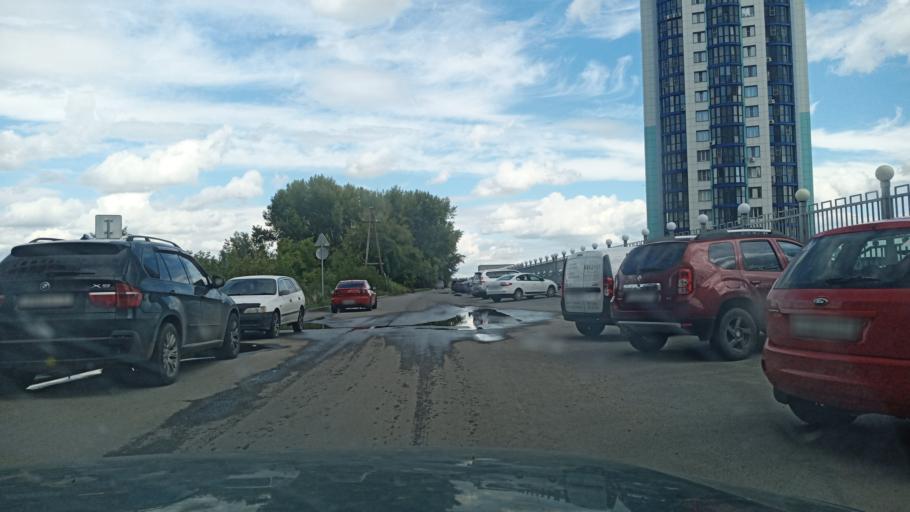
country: RU
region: Altai Krai
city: Zaton
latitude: 53.3307
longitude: 83.8049
